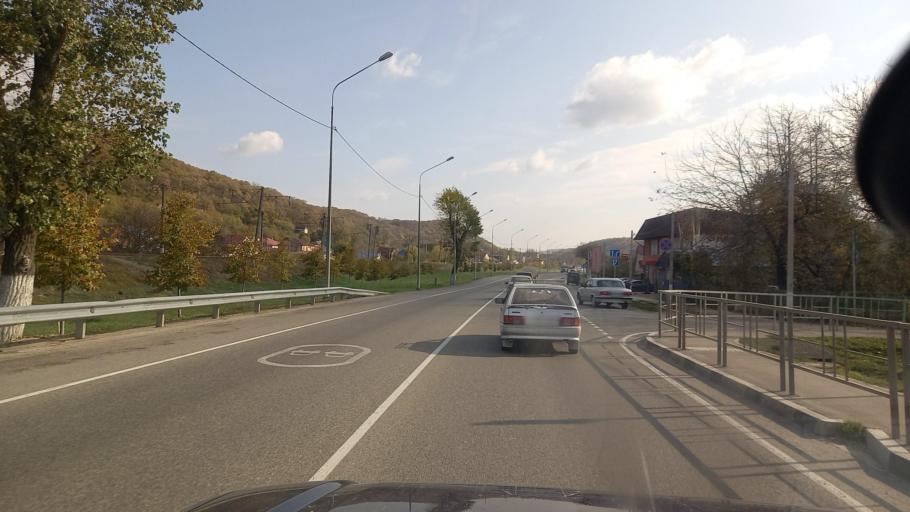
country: RU
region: Krasnodarskiy
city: Krymsk
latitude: 44.8687
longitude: 37.8752
